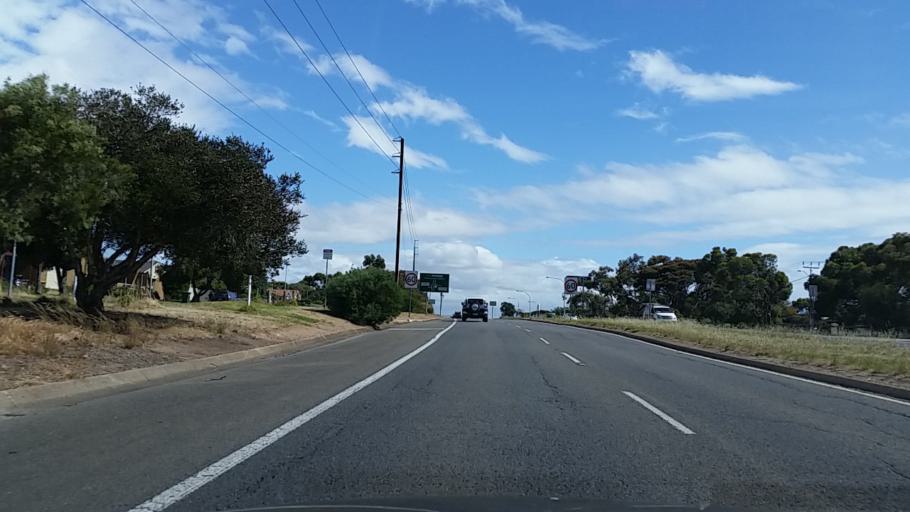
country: AU
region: South Australia
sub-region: Adelaide
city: Port Noarlunga
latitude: -35.1279
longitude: 138.4856
